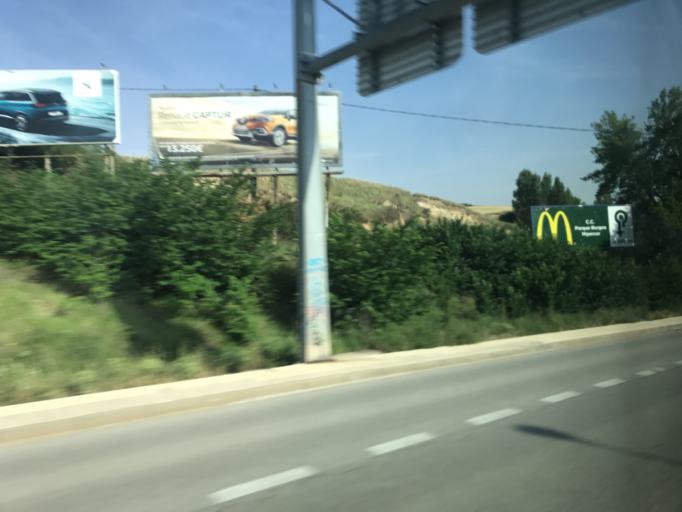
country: ES
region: Castille and Leon
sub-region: Provincia de Burgos
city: Burgos
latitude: 42.3250
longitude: -3.7014
